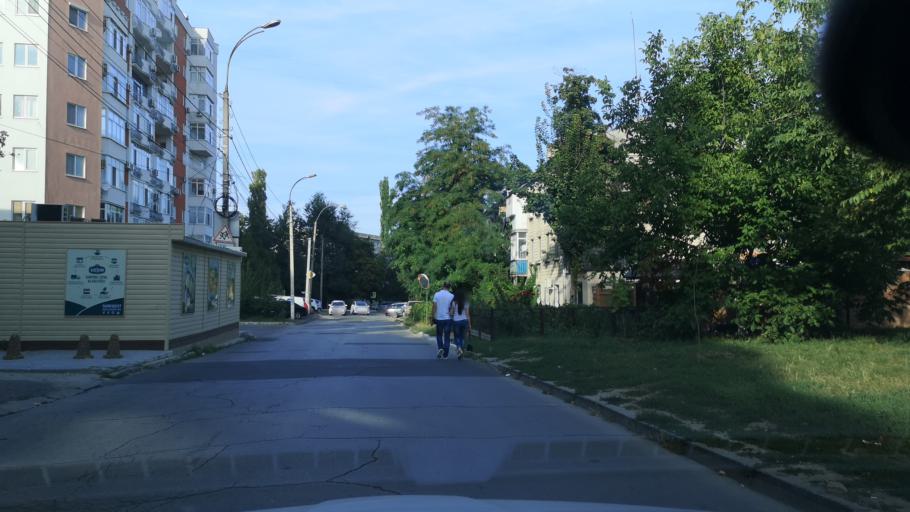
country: MD
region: Chisinau
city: Chisinau
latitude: 47.0063
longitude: 28.8484
